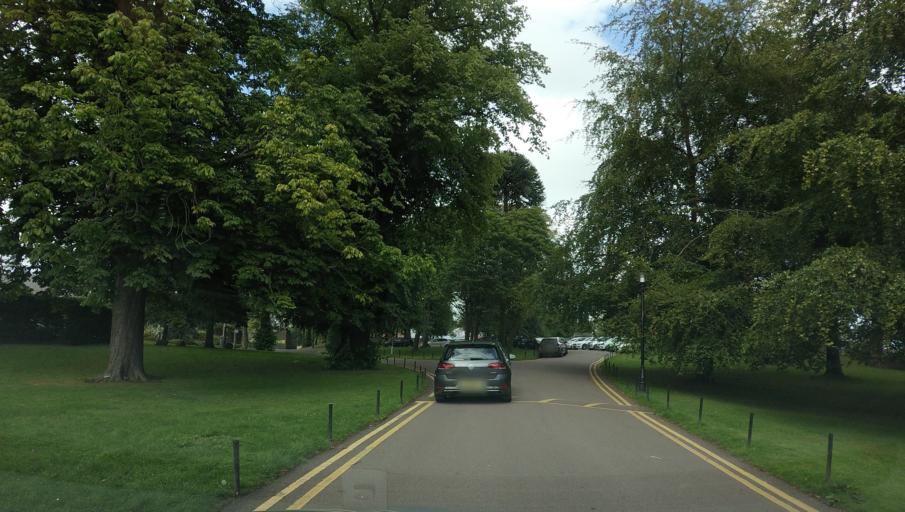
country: GB
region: Scotland
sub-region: Aberdeen City
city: Aberdeen
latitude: 57.1537
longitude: -2.1233
